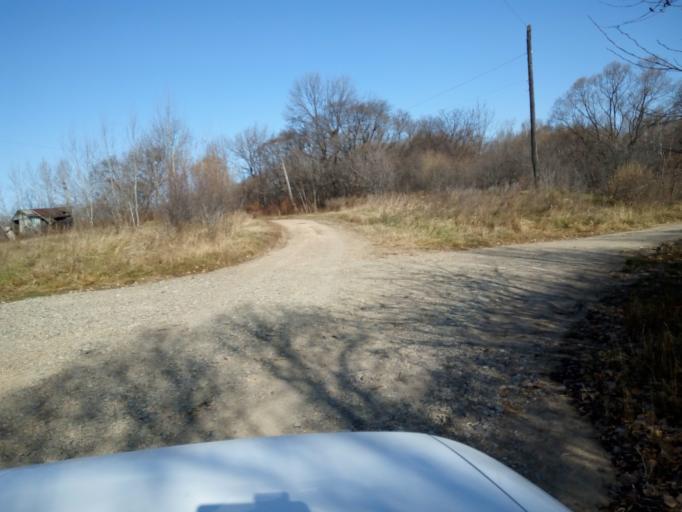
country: RU
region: Primorskiy
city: Lazo
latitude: 45.8822
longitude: 133.6408
